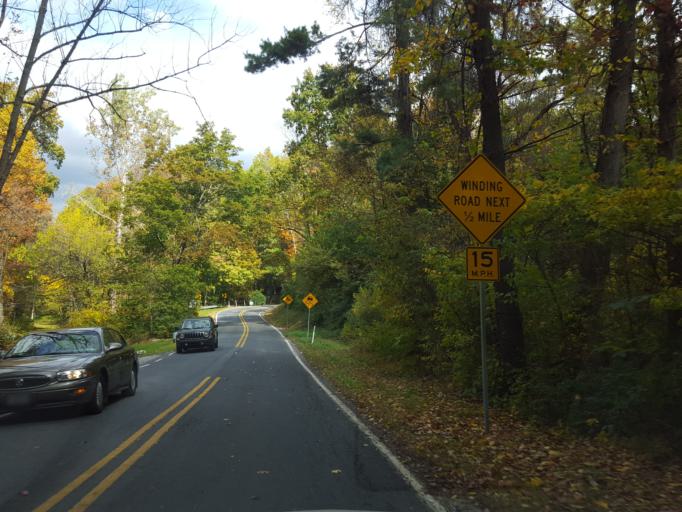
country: US
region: Pennsylvania
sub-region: York County
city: Spry
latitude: 39.9221
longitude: -76.6757
